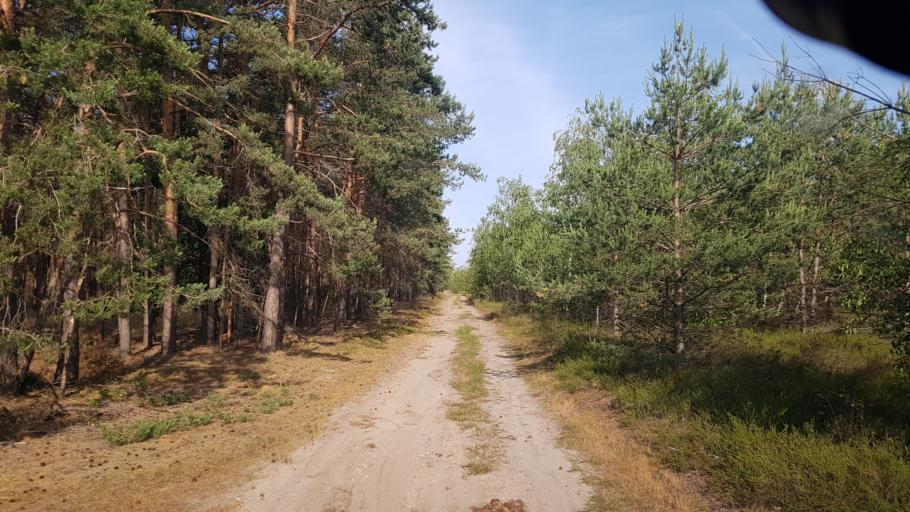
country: DE
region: Brandenburg
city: Finsterwalde
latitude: 51.6137
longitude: 13.6382
